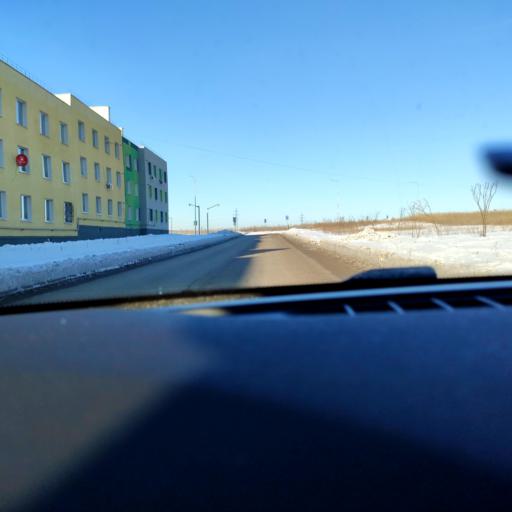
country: RU
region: Samara
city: Petra-Dubrava
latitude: 53.3066
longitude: 50.3438
